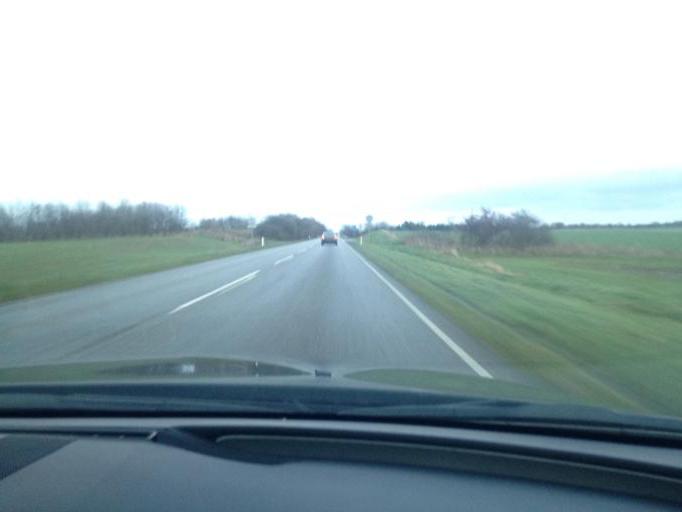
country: DK
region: South Denmark
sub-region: Kolding Kommune
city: Kolding
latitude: 55.5581
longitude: 9.4878
